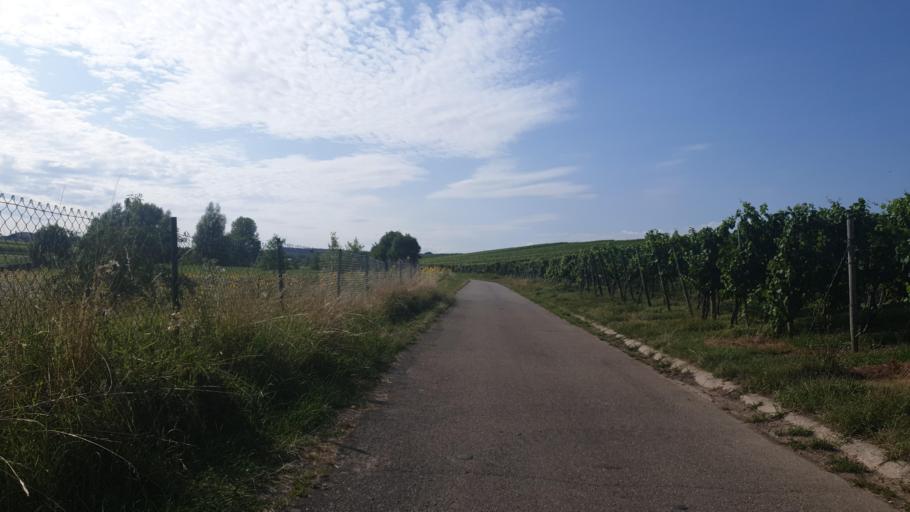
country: DE
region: Baden-Wuerttemberg
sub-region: Regierungsbezirk Stuttgart
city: Brackenheim
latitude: 49.0837
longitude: 9.0930
